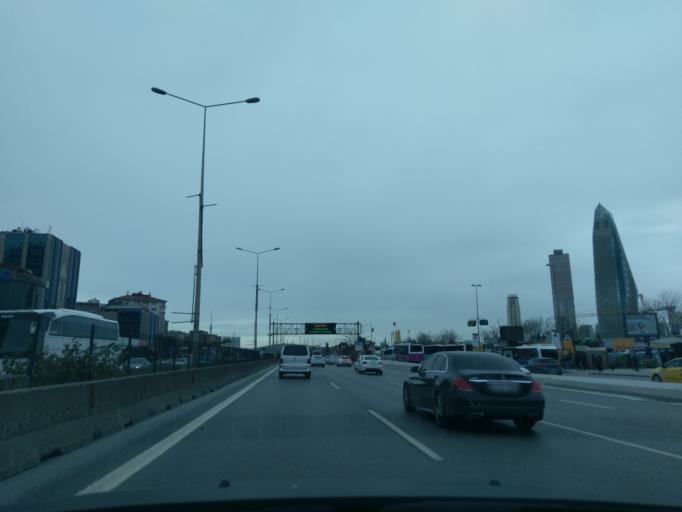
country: TR
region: Istanbul
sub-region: Atasehir
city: Atasehir
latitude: 40.9751
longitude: 29.0992
